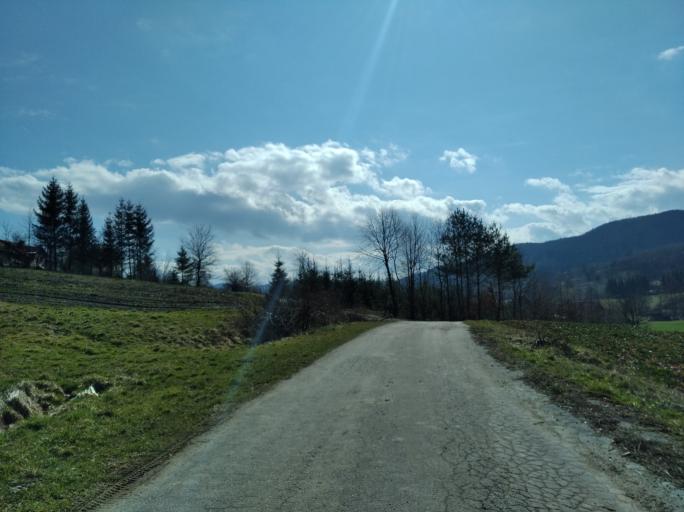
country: PL
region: Subcarpathian Voivodeship
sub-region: Powiat strzyzowski
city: Wysoka Strzyzowska
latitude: 49.8054
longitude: 21.7529
